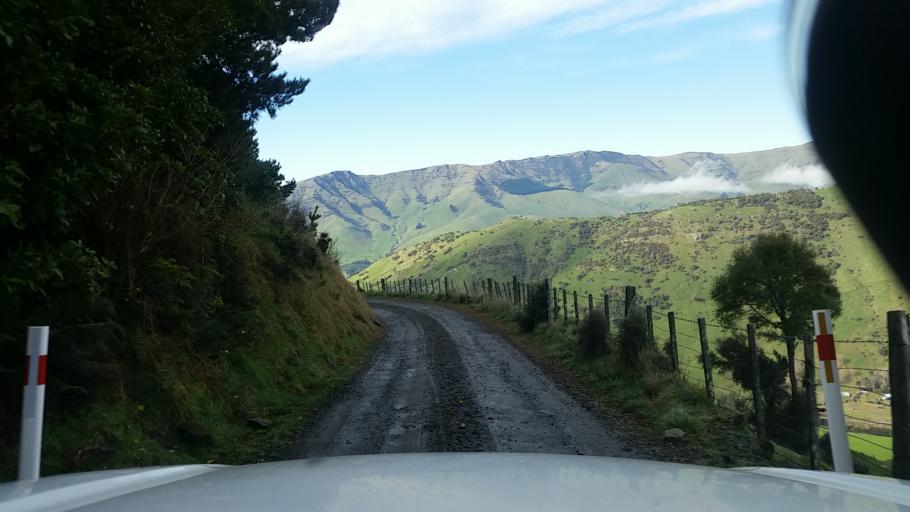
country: NZ
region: Canterbury
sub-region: Christchurch City
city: Christchurch
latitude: -43.6812
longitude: 172.8542
